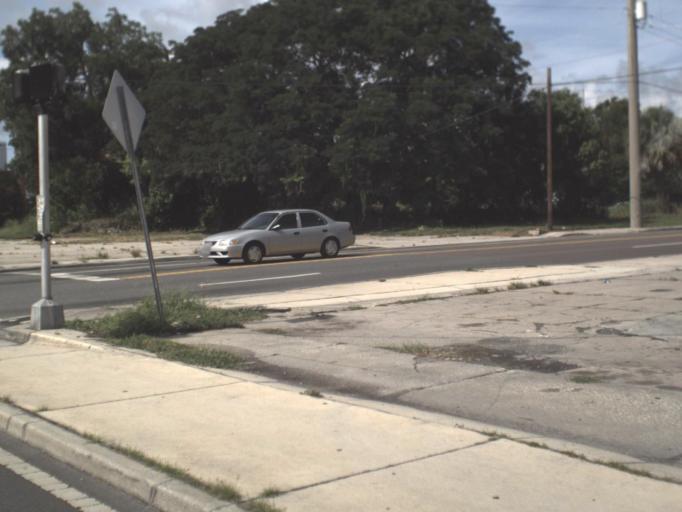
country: US
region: Florida
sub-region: Hillsborough County
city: Tampa
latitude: 27.9625
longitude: -82.4513
